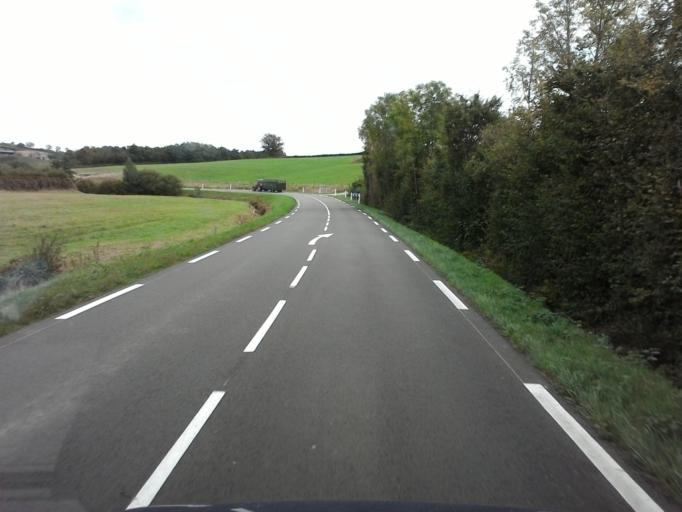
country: FR
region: Bourgogne
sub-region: Departement de Saone-et-Loire
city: Saint-Eusebe
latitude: 46.5973
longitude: 4.4897
